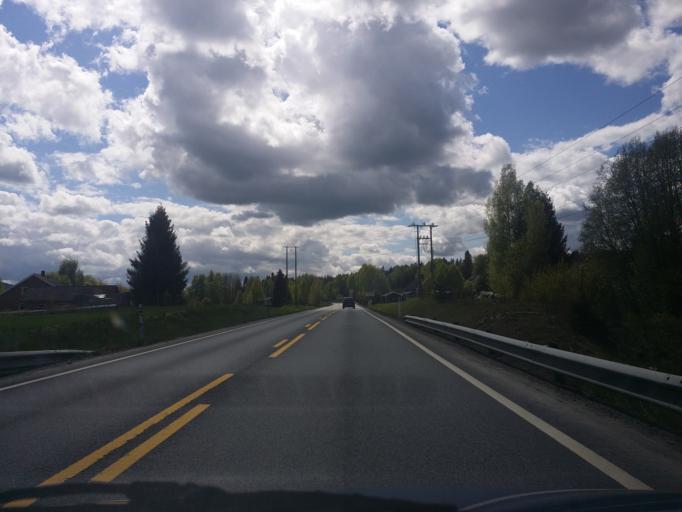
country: NO
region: Buskerud
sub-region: Modum
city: Vikersund
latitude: 59.9488
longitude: 9.9706
